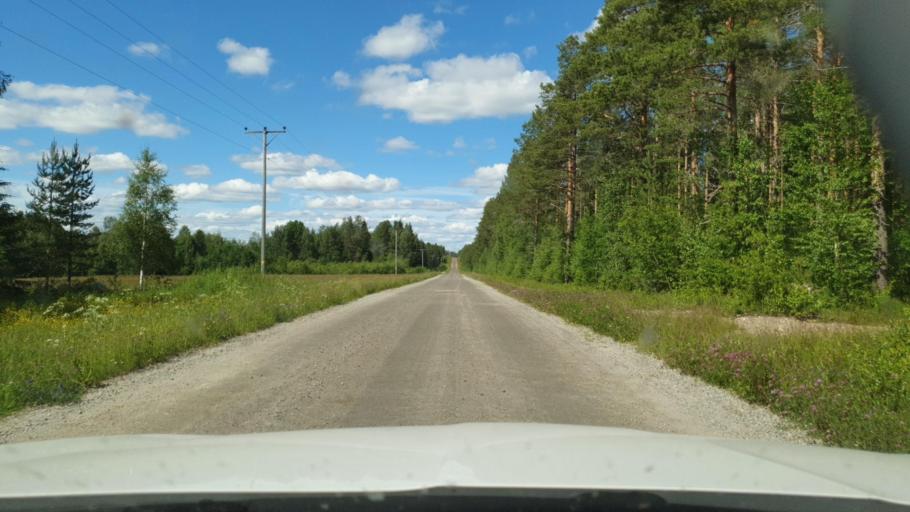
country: SE
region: Vaesterbotten
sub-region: Skelleftea Kommun
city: Backa
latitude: 65.1702
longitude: 21.1127
